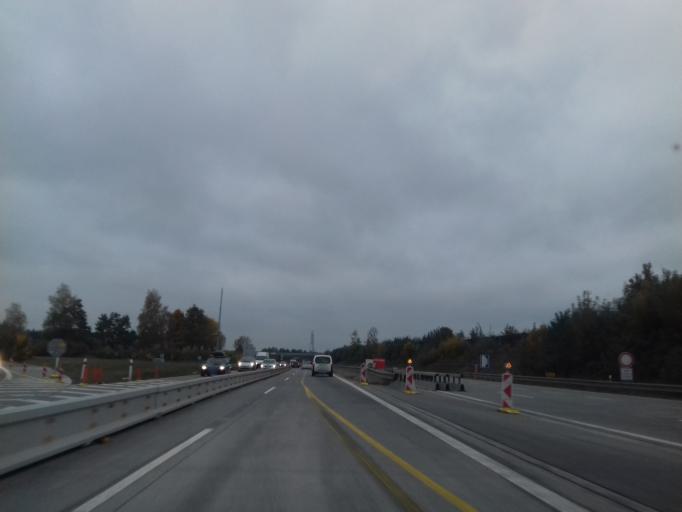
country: CZ
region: Central Bohemia
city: Trhovy Stepanov
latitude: 49.7554
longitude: 14.9708
